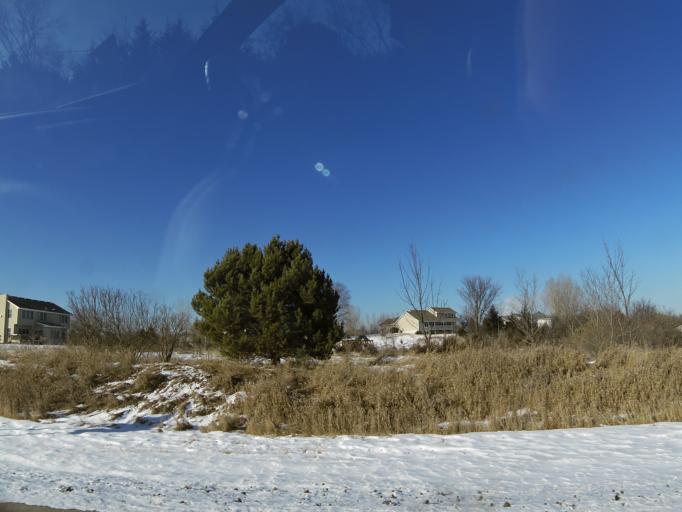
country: US
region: Minnesota
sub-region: Washington County
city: Lakeland
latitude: 44.9634
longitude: -92.7986
